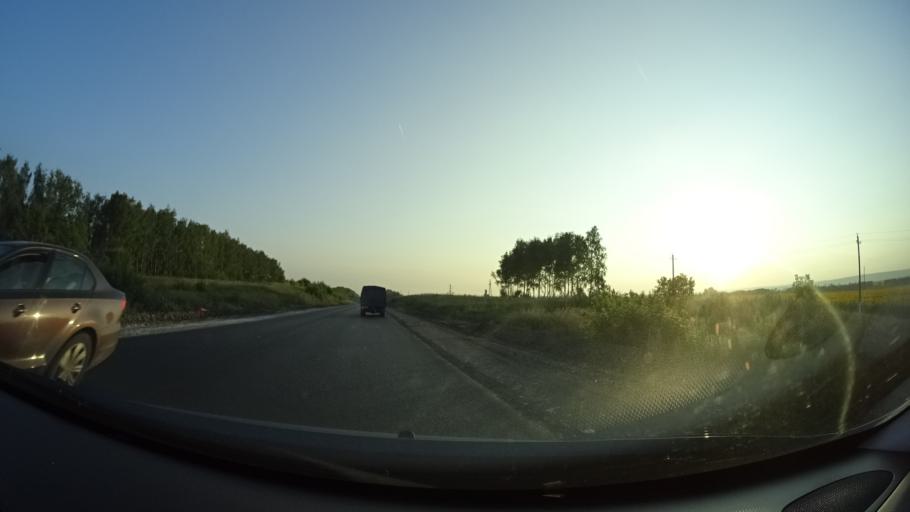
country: RU
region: Samara
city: Isakly
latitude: 53.9739
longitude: 51.4601
